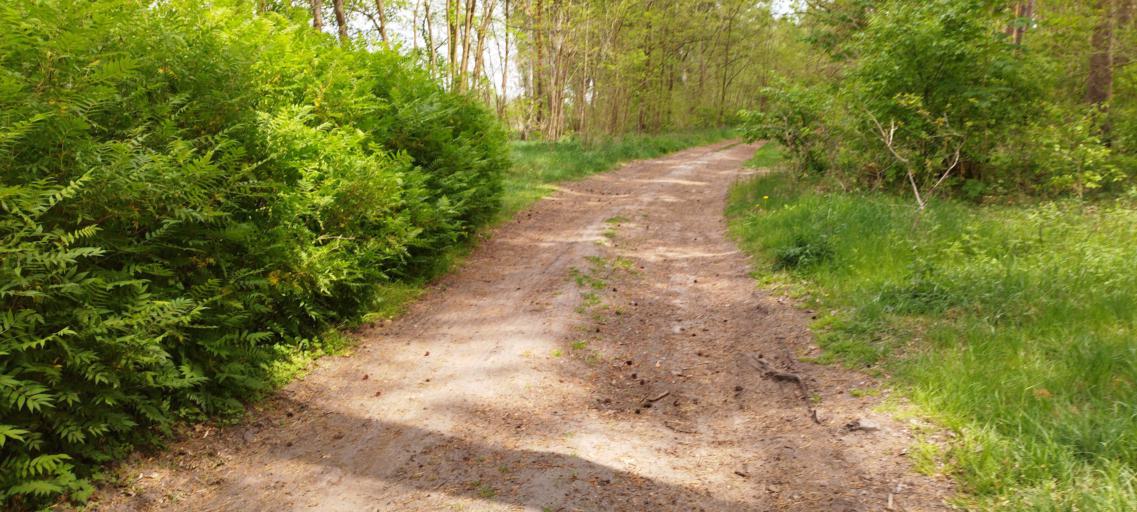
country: DE
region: Brandenburg
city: Rauen
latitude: 52.3667
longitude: 13.9960
